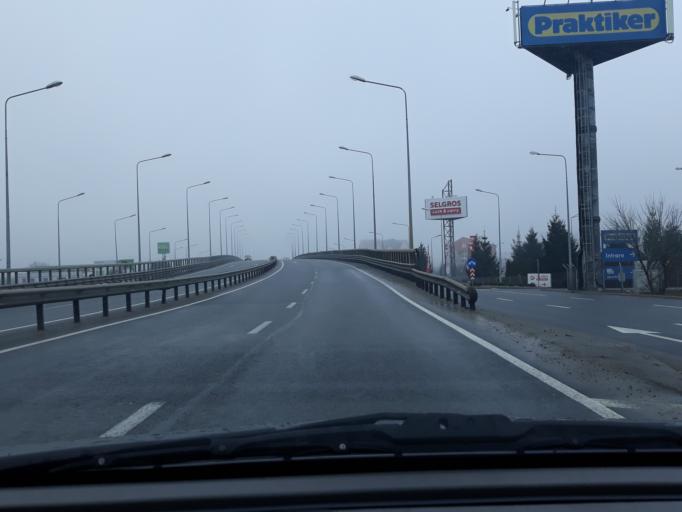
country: RO
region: Bihor
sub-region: Comuna Sanmartin
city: Sanmartin
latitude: 47.0270
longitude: 21.9622
